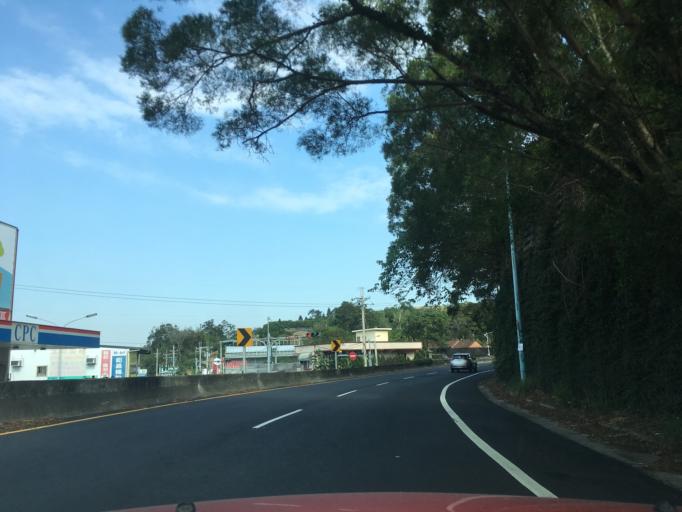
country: TW
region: Taiwan
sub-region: Hsinchu
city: Hsinchu
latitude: 24.7594
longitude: 121.0058
